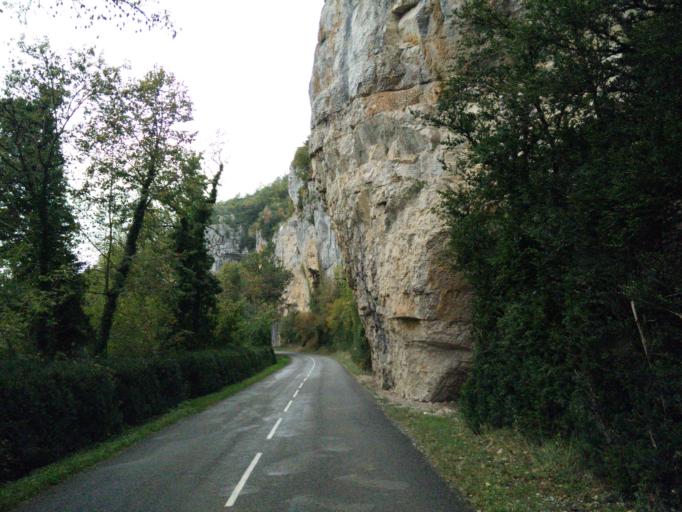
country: FR
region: Midi-Pyrenees
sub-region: Departement du Lot
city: Lalbenque
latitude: 44.4877
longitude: 1.6515
